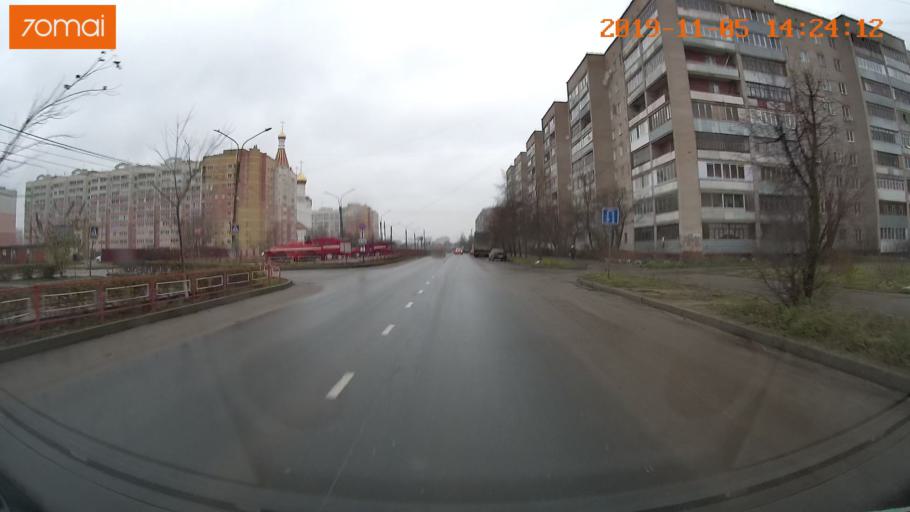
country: RU
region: Ivanovo
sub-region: Gorod Ivanovo
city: Ivanovo
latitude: 56.9674
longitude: 40.9990
